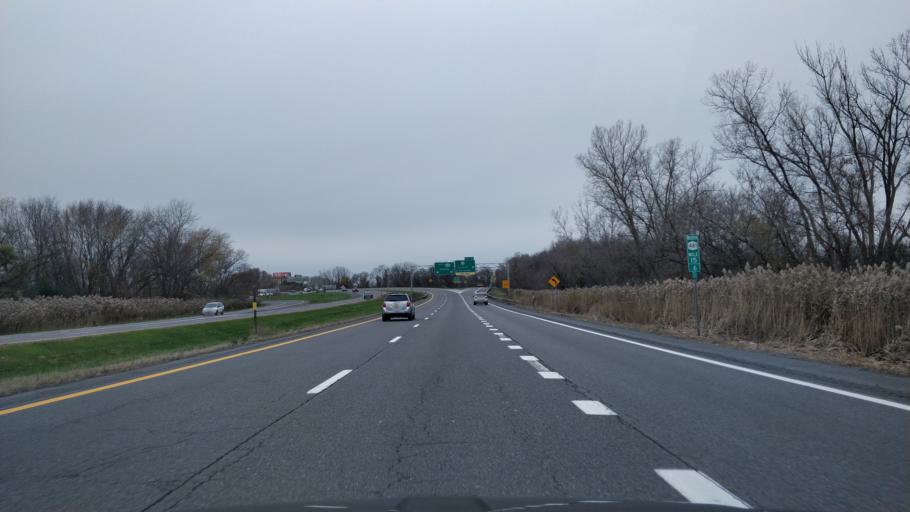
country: US
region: New York
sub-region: Onondaga County
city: North Syracuse
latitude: 43.1444
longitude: -76.1209
